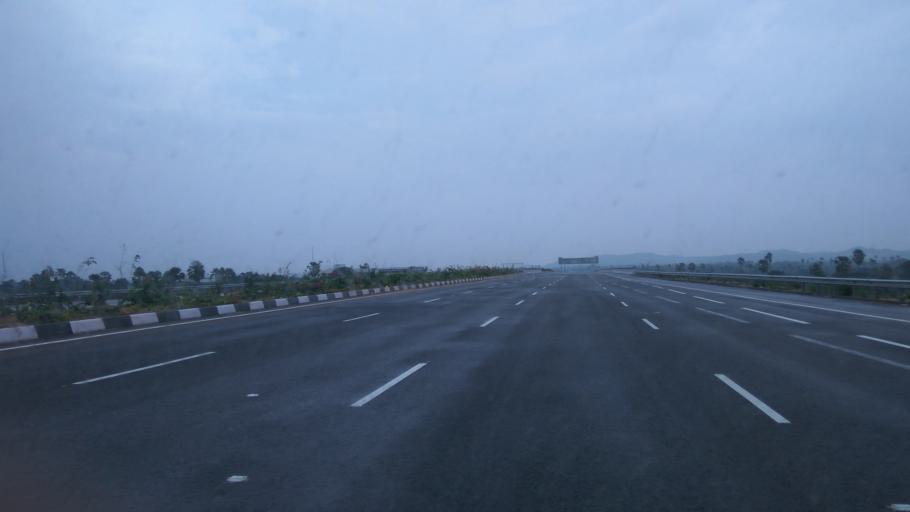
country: IN
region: Telangana
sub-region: Rangareddi
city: Ghatkesar
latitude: 17.4504
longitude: 78.6682
